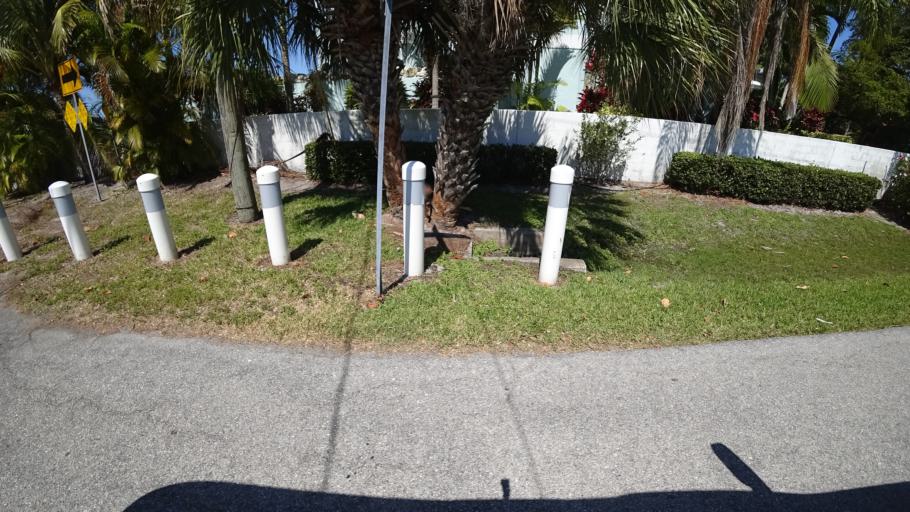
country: US
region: Florida
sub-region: Manatee County
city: Cortez
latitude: 27.4728
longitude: -82.6912
